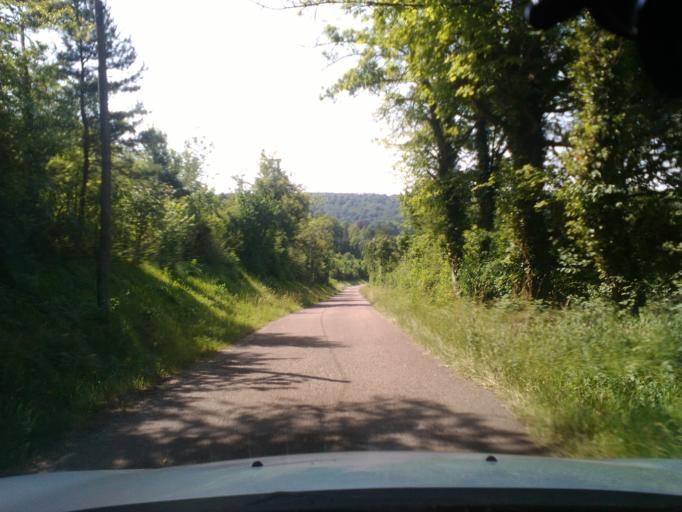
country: FR
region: Lorraine
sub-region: Departement des Vosges
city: Liffol-le-Grand
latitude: 48.3052
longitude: 5.3983
